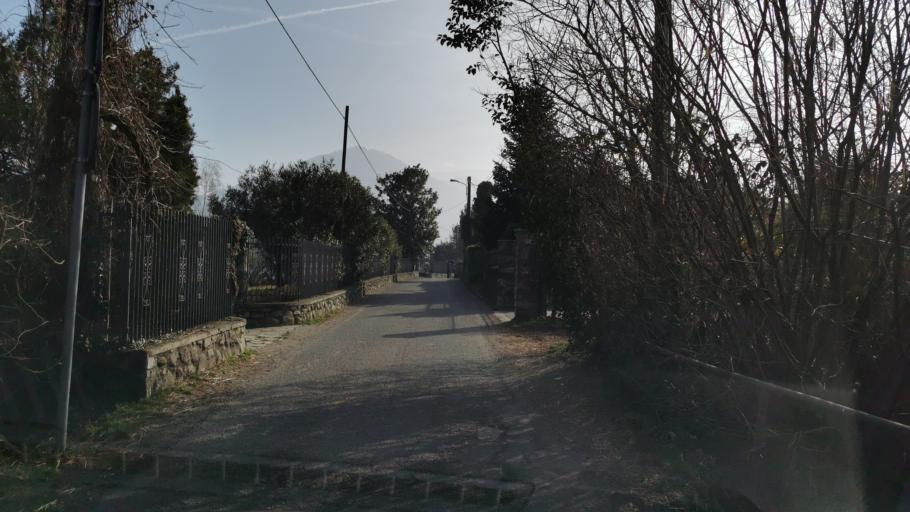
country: IT
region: Lombardy
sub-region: Provincia di Como
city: Cadenabbia
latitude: 45.9896
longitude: 9.2257
